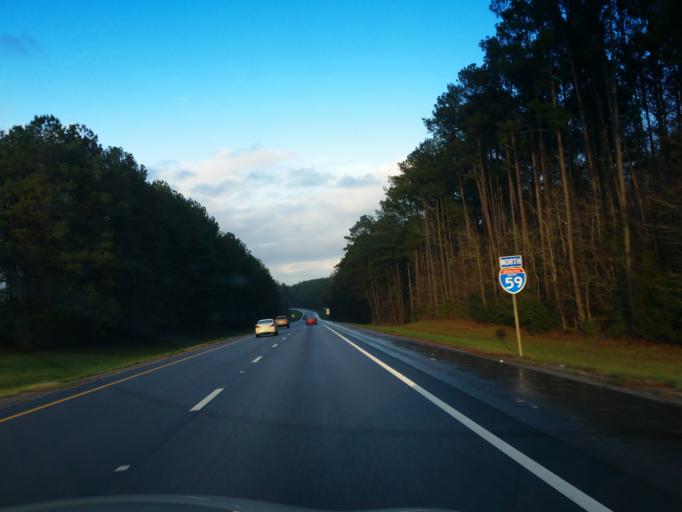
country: US
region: Mississippi
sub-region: Jones County
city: Sharon
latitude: 31.9694
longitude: -88.9618
